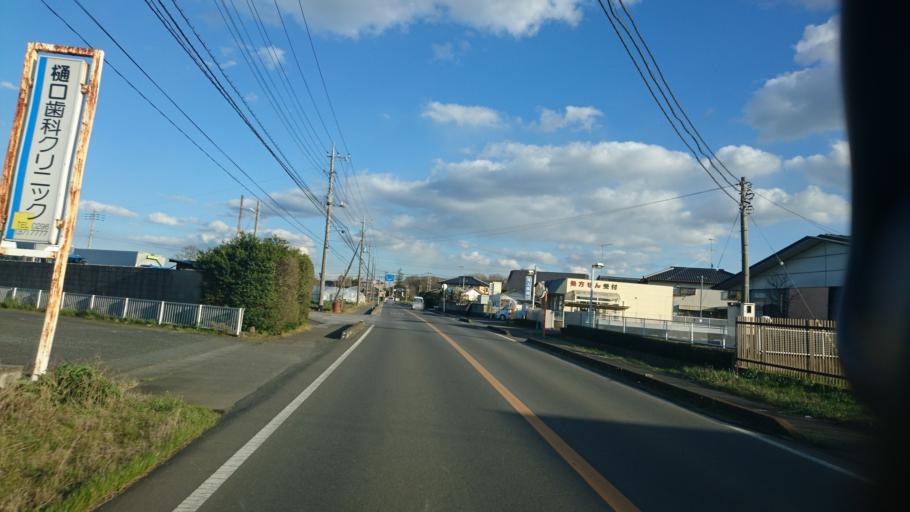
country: JP
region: Ibaraki
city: Shimodate
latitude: 36.2496
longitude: 139.9348
